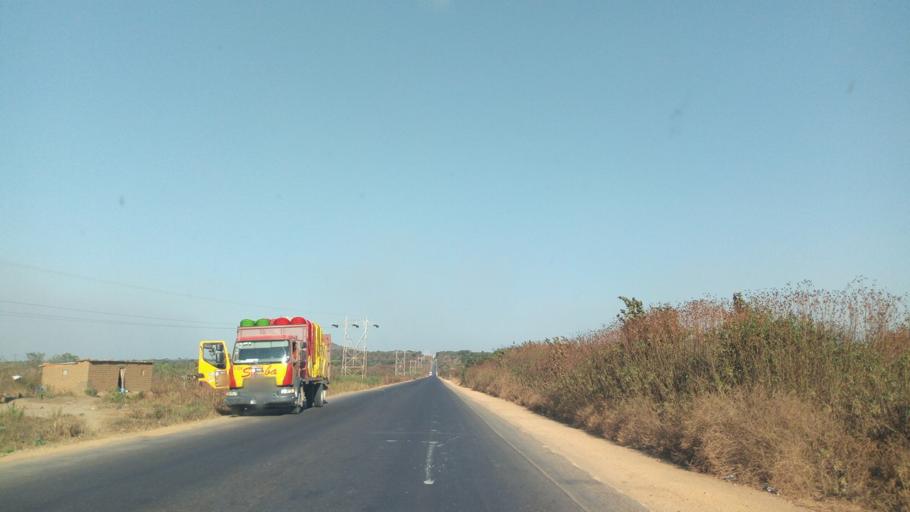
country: CD
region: Katanga
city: Likasi
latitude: -11.0506
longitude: 26.9577
